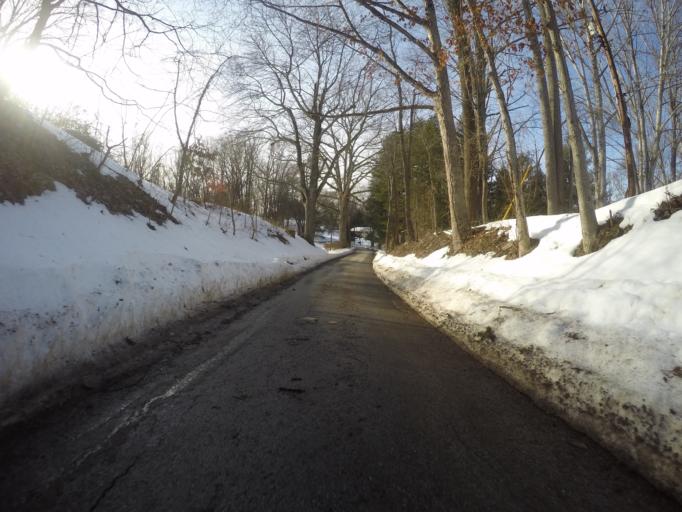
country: US
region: Maryland
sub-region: Baltimore County
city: Hunt Valley
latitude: 39.5486
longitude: -76.6482
